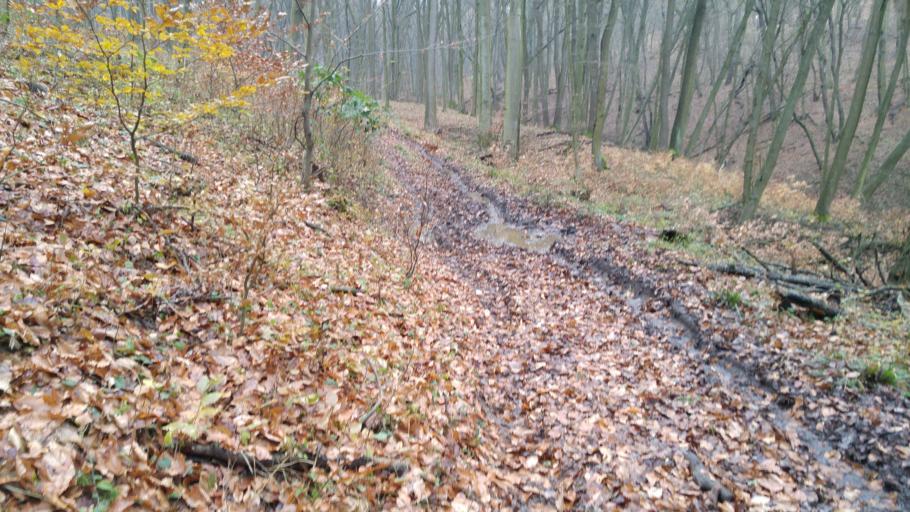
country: HU
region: Pest
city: Nagymaros
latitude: 47.8338
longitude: 18.9598
